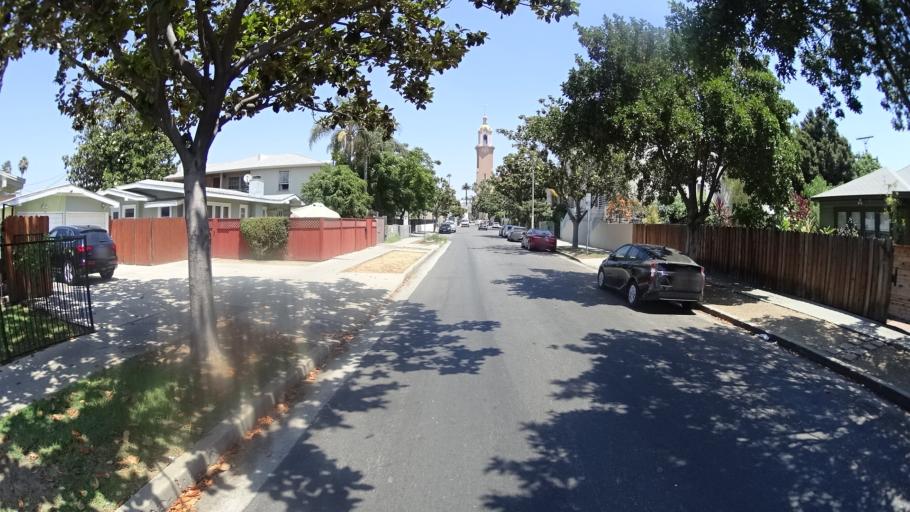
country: US
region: California
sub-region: Los Angeles County
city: Hollywood
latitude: 34.0964
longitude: -118.3354
